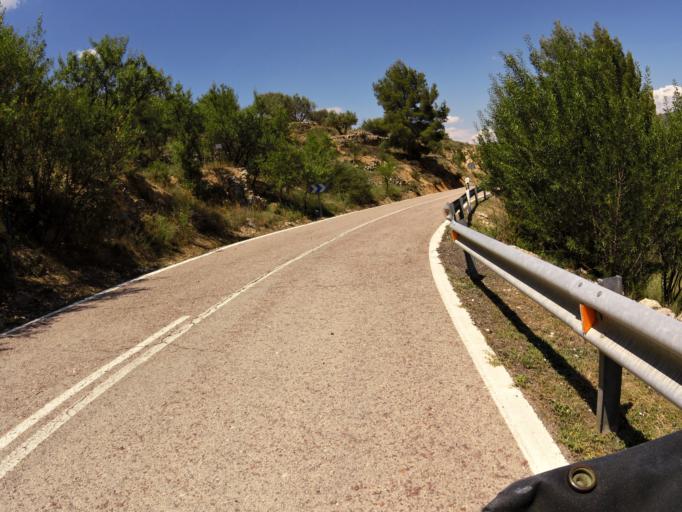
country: ES
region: Valencia
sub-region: Provincia de Valencia
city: Casas Bajas
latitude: 40.0188
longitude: -1.2654
